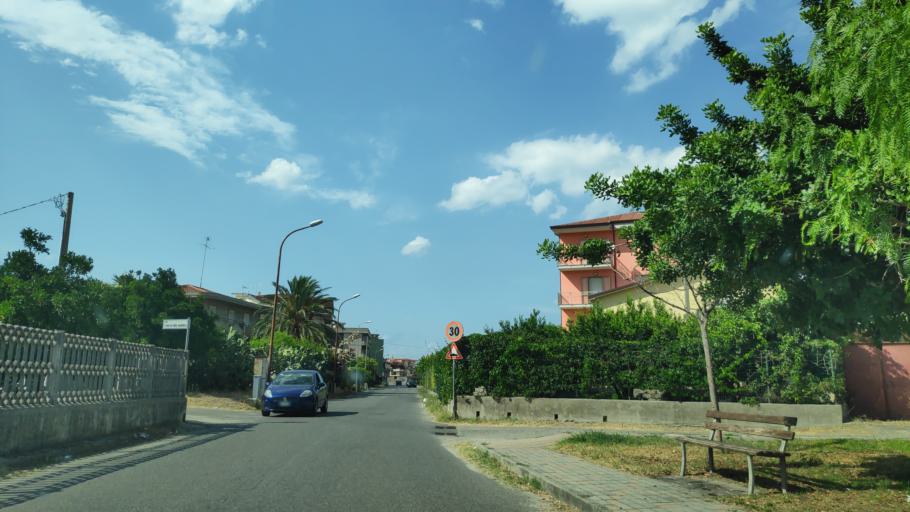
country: IT
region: Calabria
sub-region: Provincia di Catanzaro
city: Marina di Davoli
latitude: 38.6651
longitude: 16.5421
